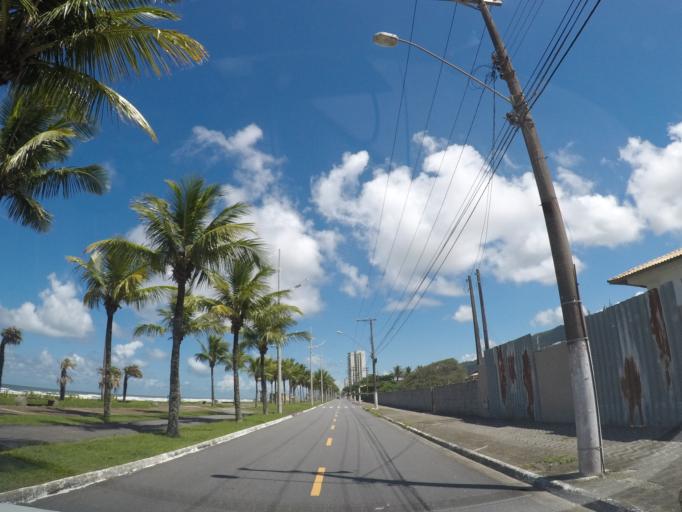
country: BR
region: Sao Paulo
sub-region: Mongagua
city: Mongagua
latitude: -24.0762
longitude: -46.5795
